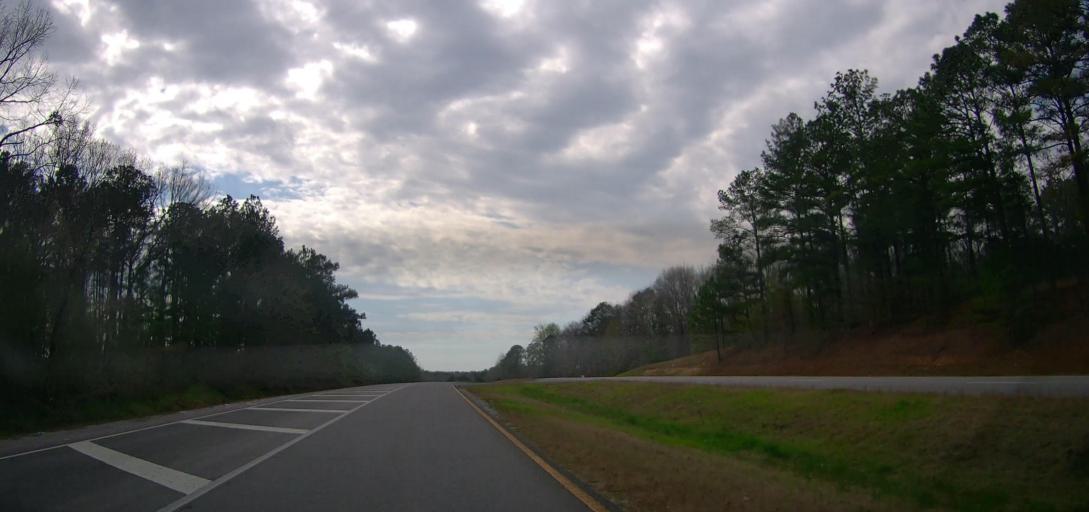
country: US
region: Alabama
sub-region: Marion County
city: Winfield
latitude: 33.9301
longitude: -87.7516
